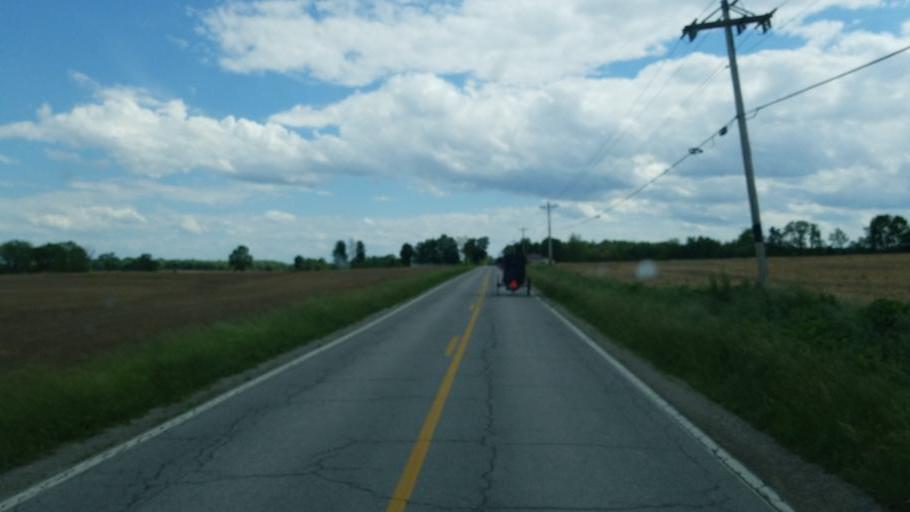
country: US
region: Ohio
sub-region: Huron County
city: Plymouth
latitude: 41.0506
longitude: -82.6095
